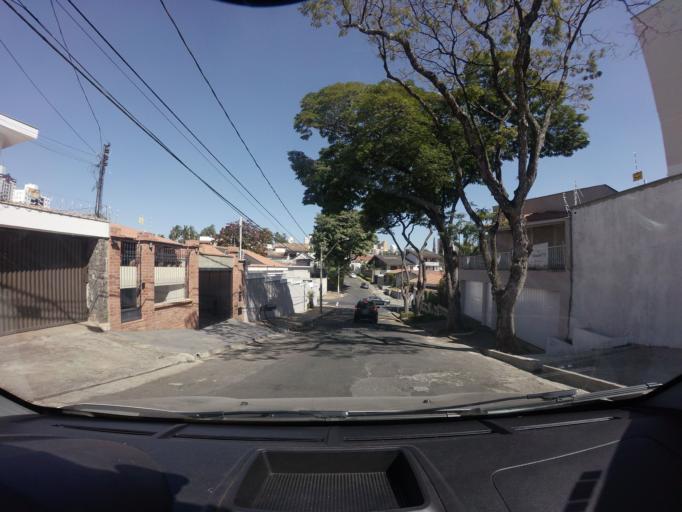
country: BR
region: Sao Paulo
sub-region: Piracicaba
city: Piracicaba
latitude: -22.7180
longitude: -47.6423
